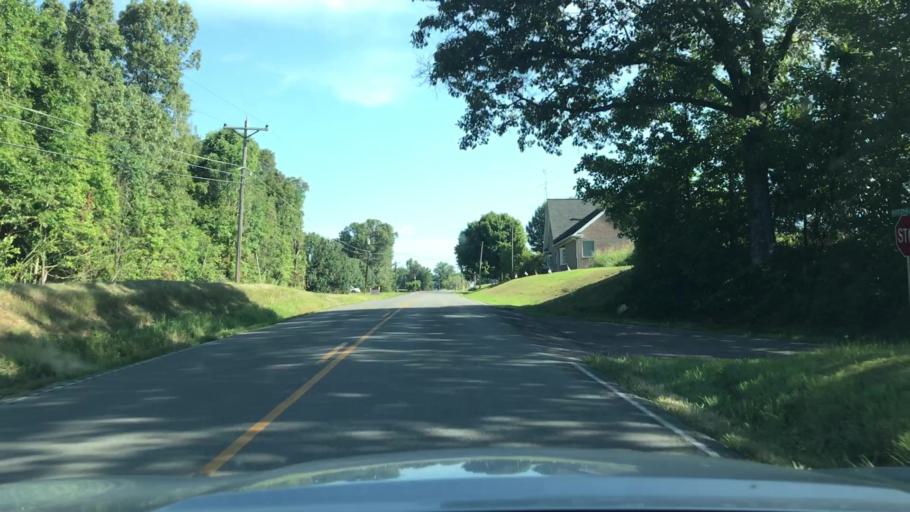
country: US
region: Kentucky
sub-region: Muhlenberg County
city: Greenville
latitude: 37.1547
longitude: -87.1418
